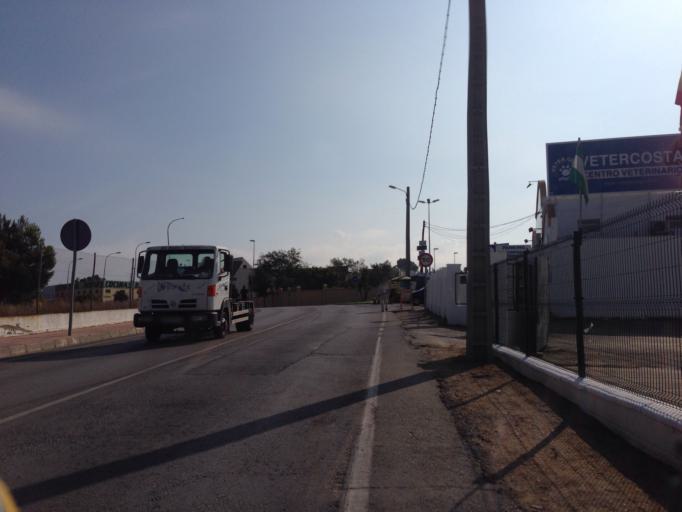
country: ES
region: Andalusia
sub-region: Provincia de Cadiz
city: Chiclana de la Frontera
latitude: 36.4409
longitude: -6.1431
